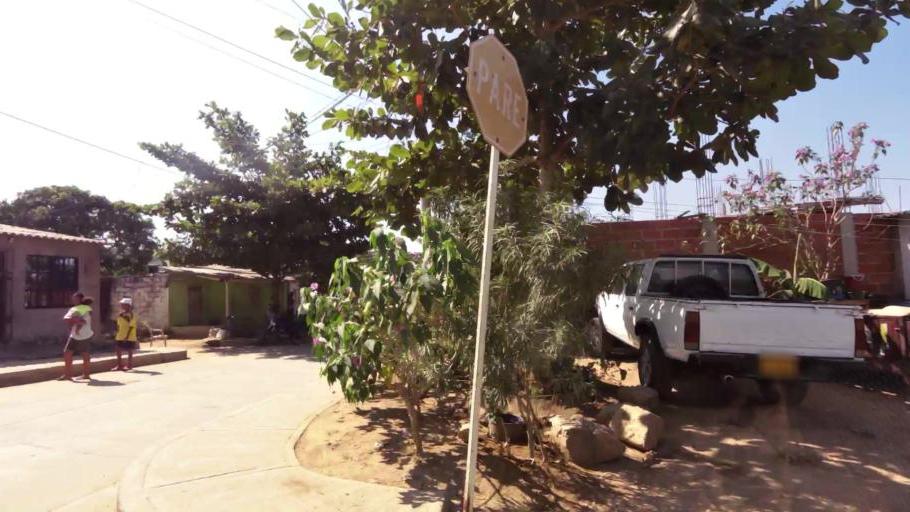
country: CO
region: Bolivar
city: Cartagena
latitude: 10.3689
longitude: -75.4974
